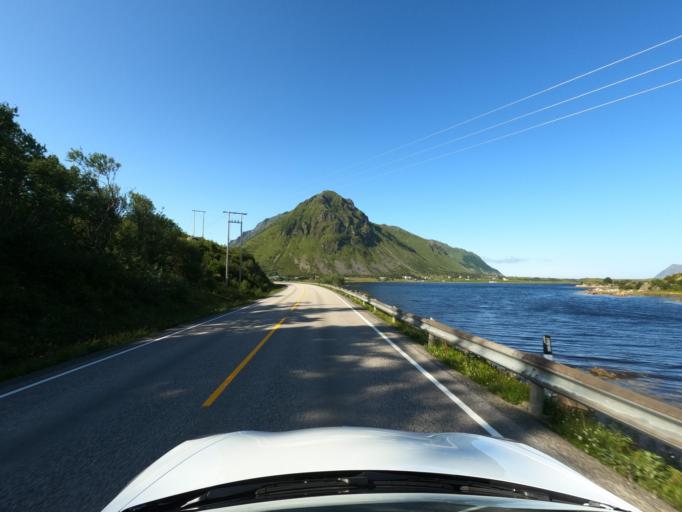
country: NO
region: Nordland
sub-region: Vestvagoy
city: Evjen
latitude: 68.2659
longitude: 13.9789
